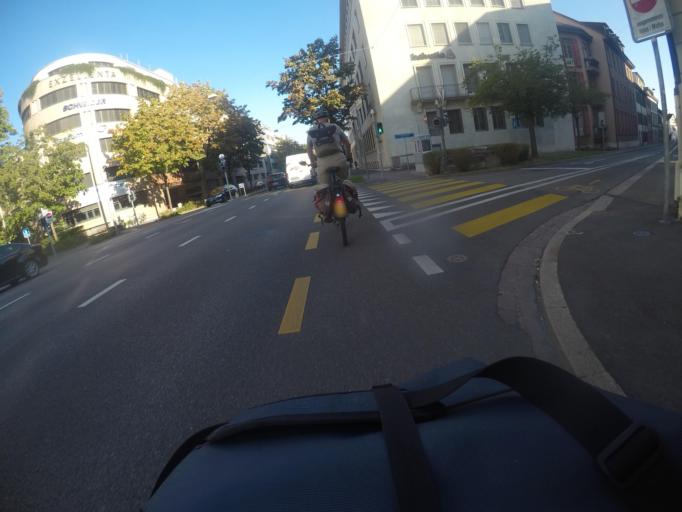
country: CH
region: Basel-City
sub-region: Basel-Stadt
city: Basel
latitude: 47.5540
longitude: 7.5859
